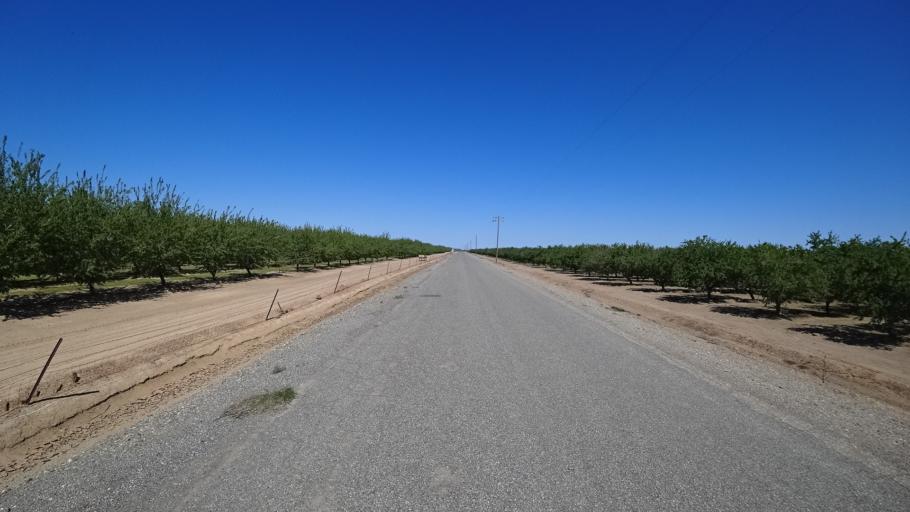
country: US
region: California
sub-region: Glenn County
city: Orland
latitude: 39.6401
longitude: -122.2347
